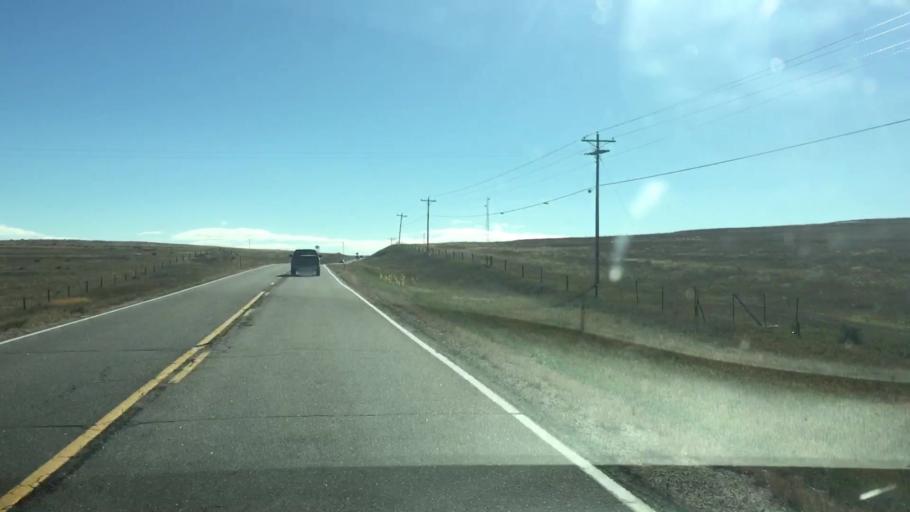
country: US
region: Colorado
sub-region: Elbert County
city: Kiowa
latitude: 39.3500
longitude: -104.4864
